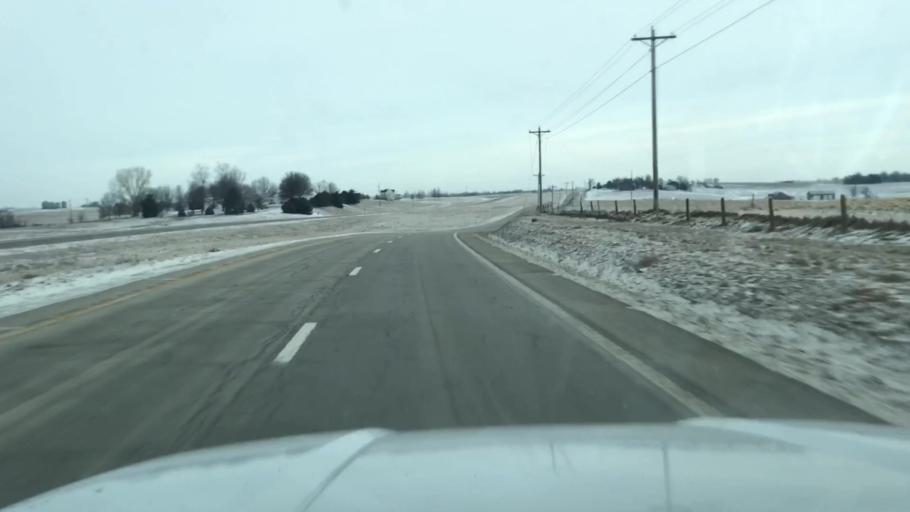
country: US
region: Missouri
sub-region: Andrew County
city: Savannah
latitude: 39.9840
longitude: -94.8798
